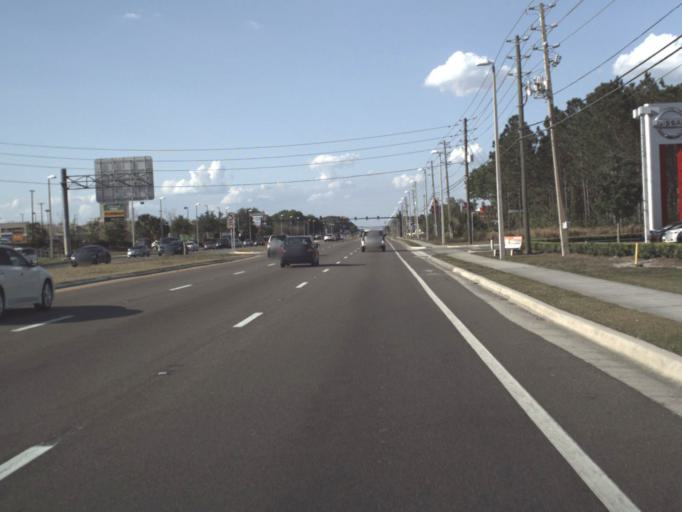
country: US
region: Florida
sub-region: Orange County
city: Southchase
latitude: 28.3804
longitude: -81.4044
